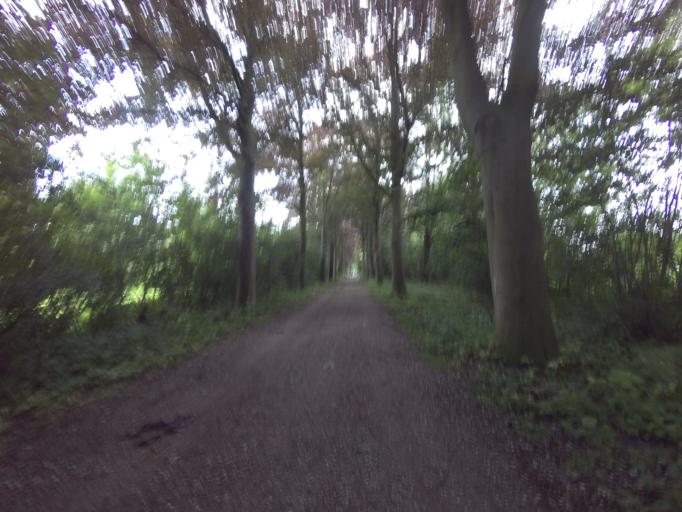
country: NL
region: Utrecht
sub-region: Gemeente Bunnik
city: Bunnik
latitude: 52.0740
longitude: 5.1727
